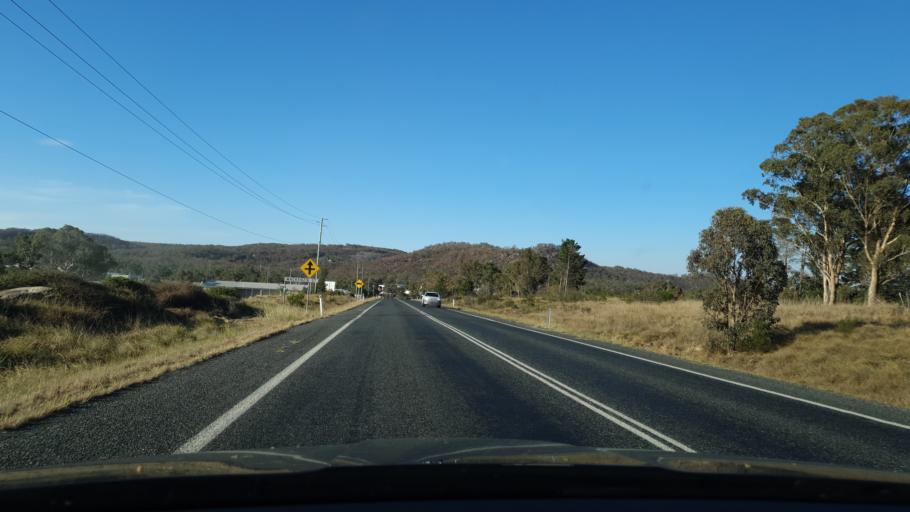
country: AU
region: Queensland
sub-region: Southern Downs
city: Stanthorpe
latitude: -28.6591
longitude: 151.9167
